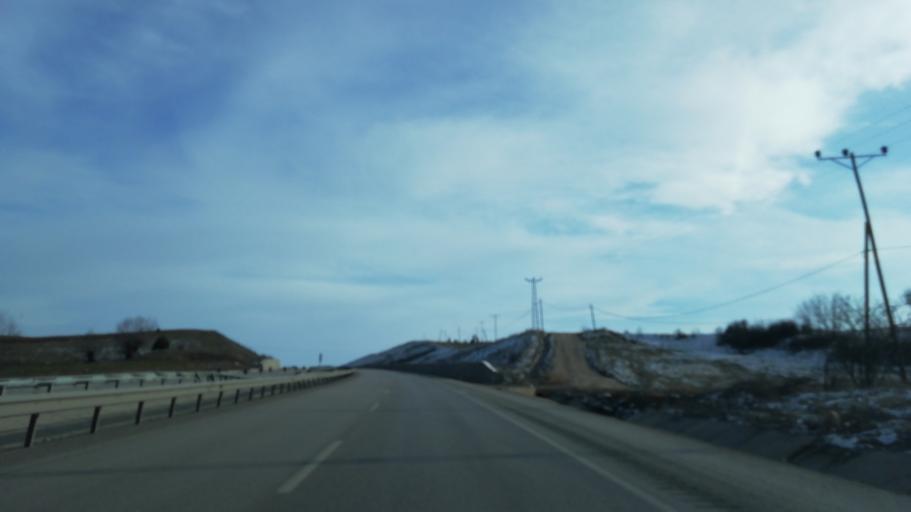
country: TR
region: Karabuk
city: Eskipazar
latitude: 40.9410
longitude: 32.5612
